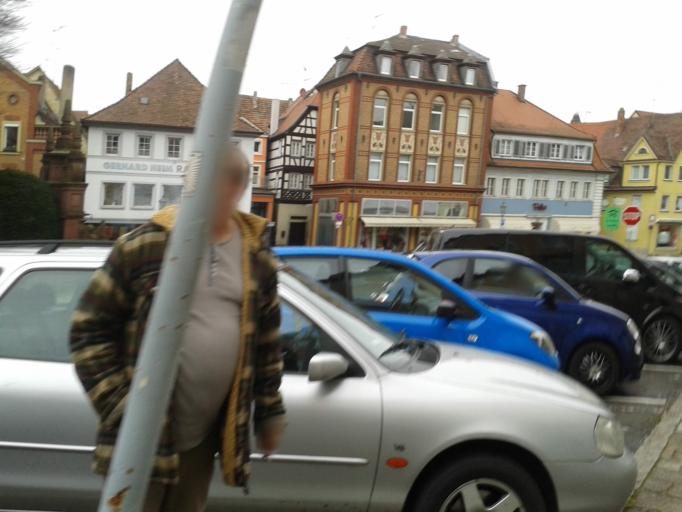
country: DE
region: Bavaria
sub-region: Regierungsbezirk Unterfranken
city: Kitzingen
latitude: 49.7380
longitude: 10.1603
